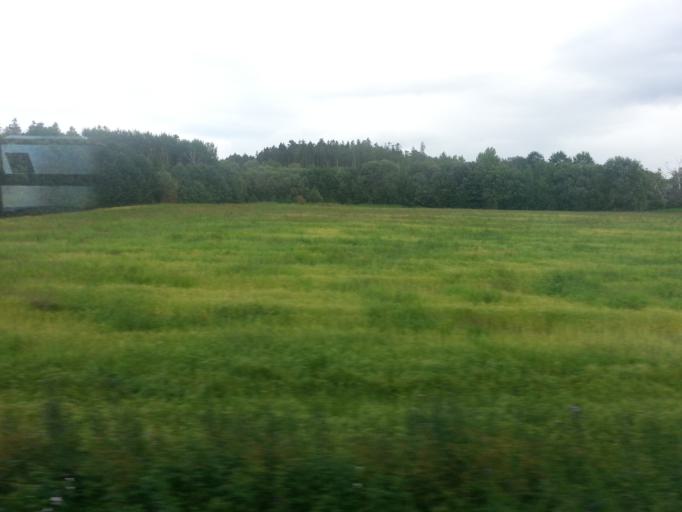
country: NO
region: Sor-Trondelag
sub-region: Malvik
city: Malvik
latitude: 63.4373
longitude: 10.5819
